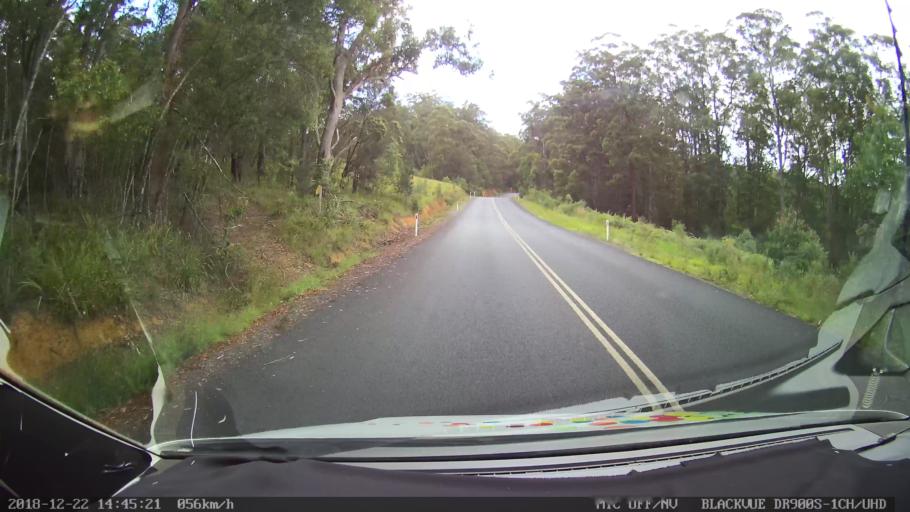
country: AU
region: New South Wales
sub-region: Bellingen
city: Dorrigo
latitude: -30.1698
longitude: 152.5698
